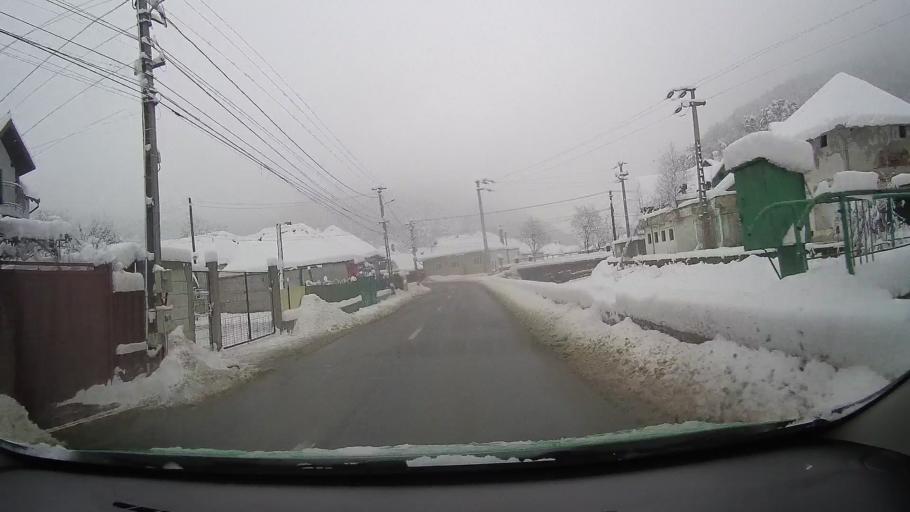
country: RO
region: Sibiu
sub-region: Comuna Tilisca
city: Tilisca
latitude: 45.7984
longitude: 23.8610
